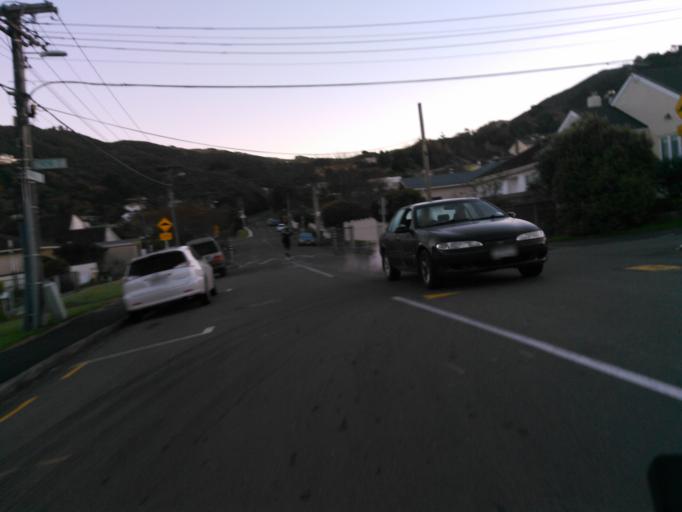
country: NZ
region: Wellington
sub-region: Wellington City
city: Kelburn
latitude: -41.2829
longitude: 174.7366
